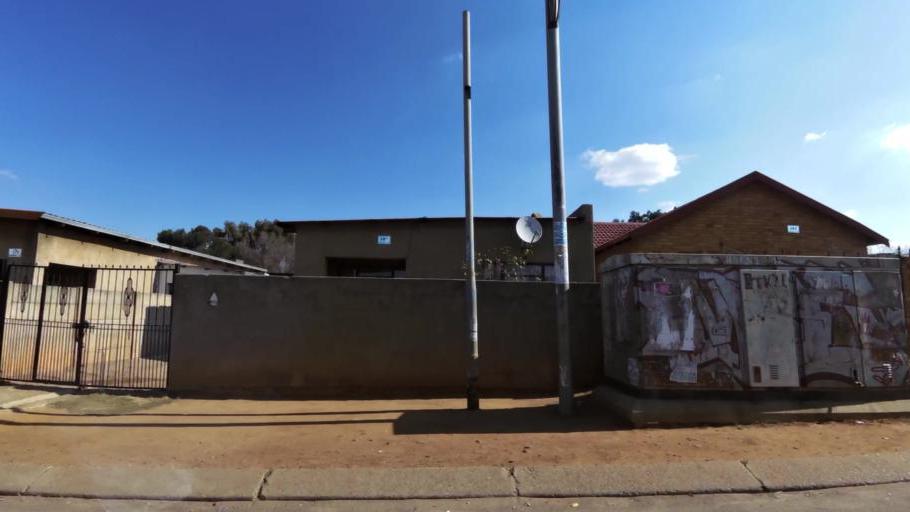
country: ZA
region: Gauteng
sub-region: City of Johannesburg Metropolitan Municipality
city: Soweto
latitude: -26.2376
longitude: 27.8792
